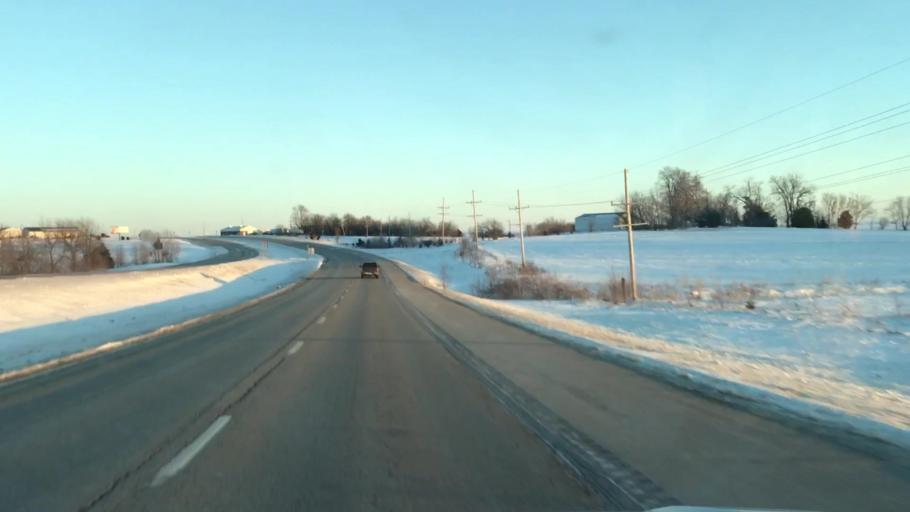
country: US
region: Missouri
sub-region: Clinton County
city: Cameron
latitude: 39.7571
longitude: -94.3440
